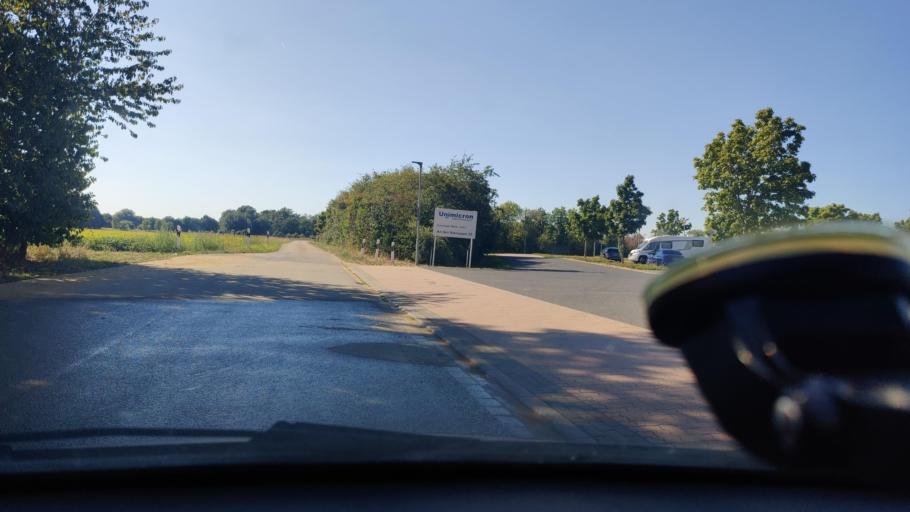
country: DE
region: North Rhine-Westphalia
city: Geldern
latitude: 51.5037
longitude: 6.3180
